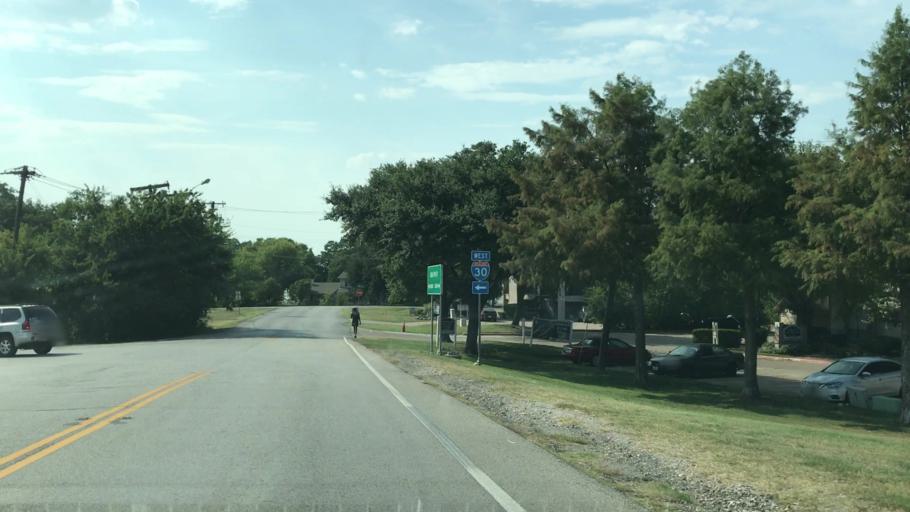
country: US
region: Texas
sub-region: Dallas County
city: Rowlett
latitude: 32.8655
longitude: -96.5447
